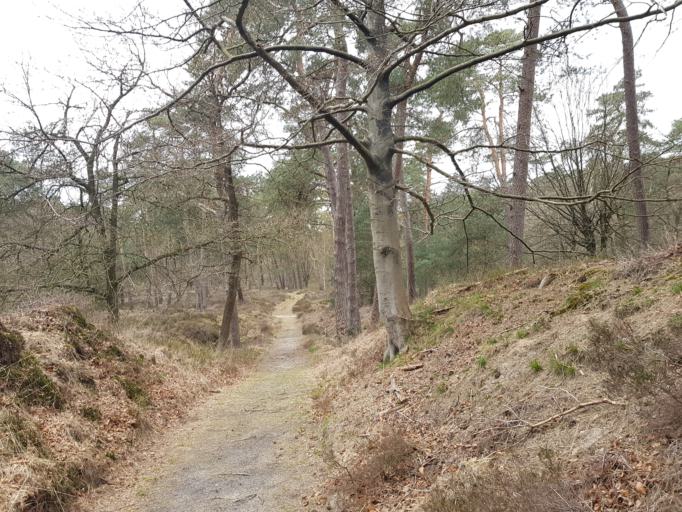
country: NL
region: Gelderland
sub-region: Gemeente Apeldoorn
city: Apeldoorn
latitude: 52.2338
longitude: 5.9122
